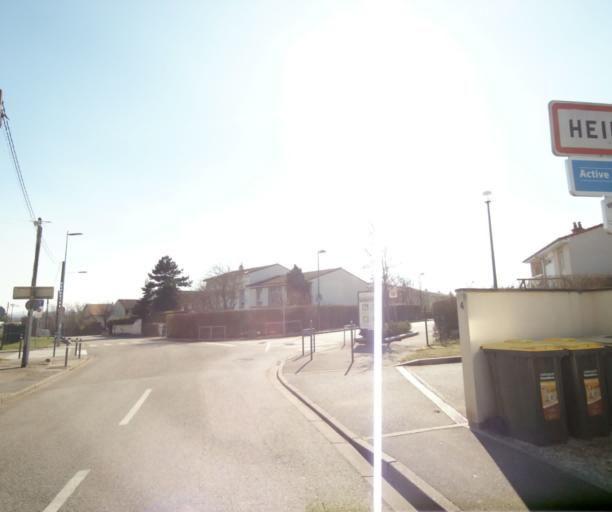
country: FR
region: Lorraine
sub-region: Departement de Meurthe-et-Moselle
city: Heillecourt
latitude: 48.6601
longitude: 6.1973
